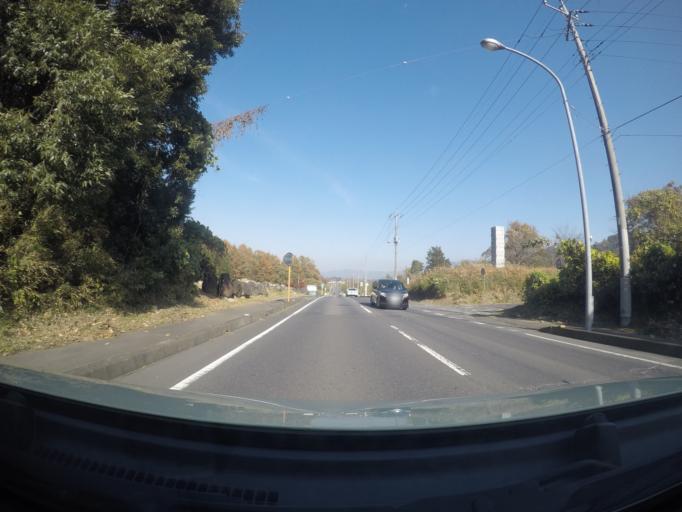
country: JP
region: Ibaraki
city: Makabe
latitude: 36.2425
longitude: 140.0669
